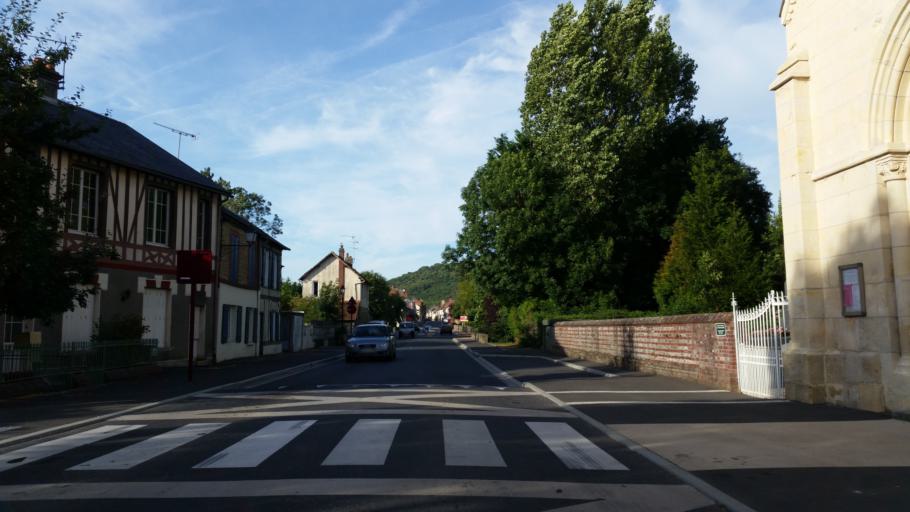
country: FR
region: Lower Normandy
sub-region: Departement du Calvados
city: Cambremer
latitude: 49.1147
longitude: 0.0116
